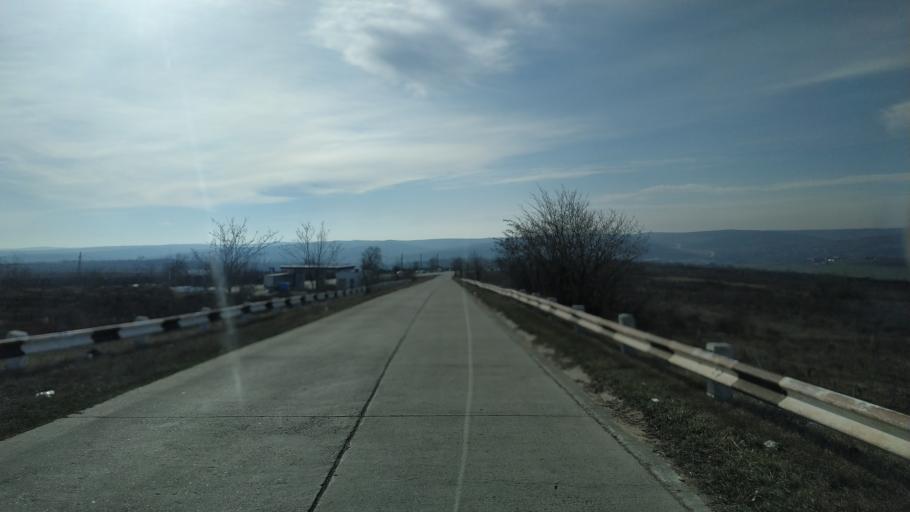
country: MD
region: Chisinau
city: Chisinau
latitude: 46.9420
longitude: 28.8659
